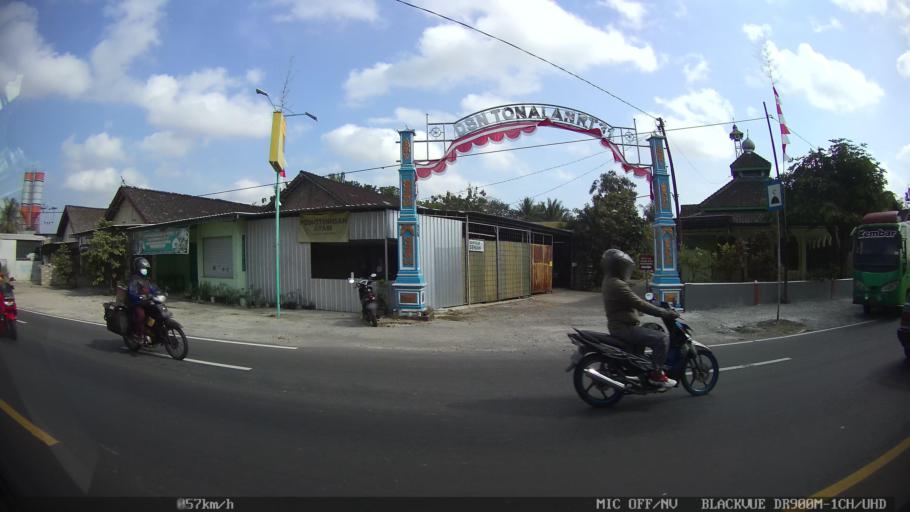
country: ID
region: Daerah Istimewa Yogyakarta
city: Godean
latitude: -7.8171
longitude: 110.2471
